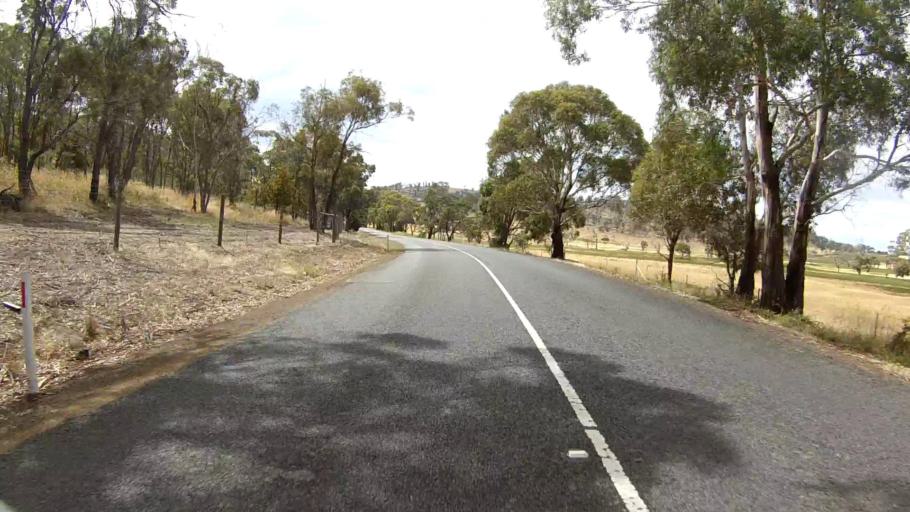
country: AU
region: Tasmania
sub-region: Sorell
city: Sorell
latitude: -42.8825
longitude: 147.6701
